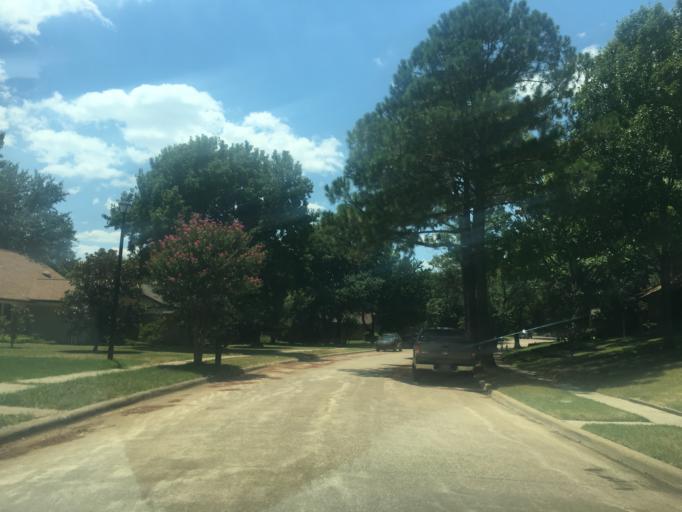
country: US
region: Texas
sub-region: Denton County
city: Lewisville
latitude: 33.0243
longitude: -97.0035
